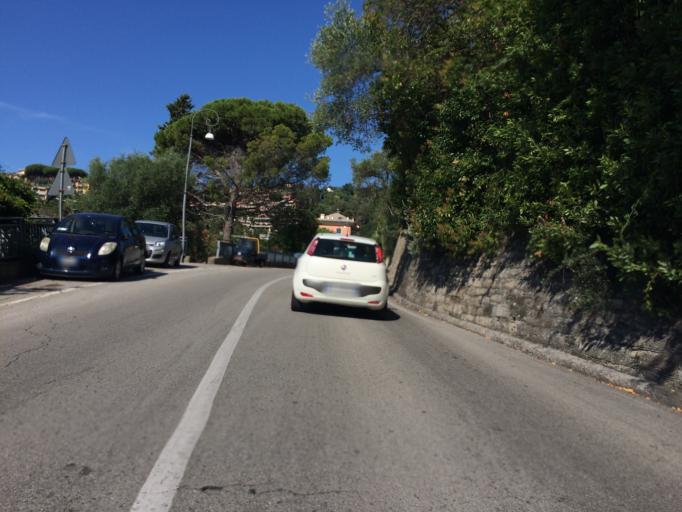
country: IT
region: Liguria
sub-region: Provincia di Genova
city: Rapallo
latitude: 44.3448
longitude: 9.2182
